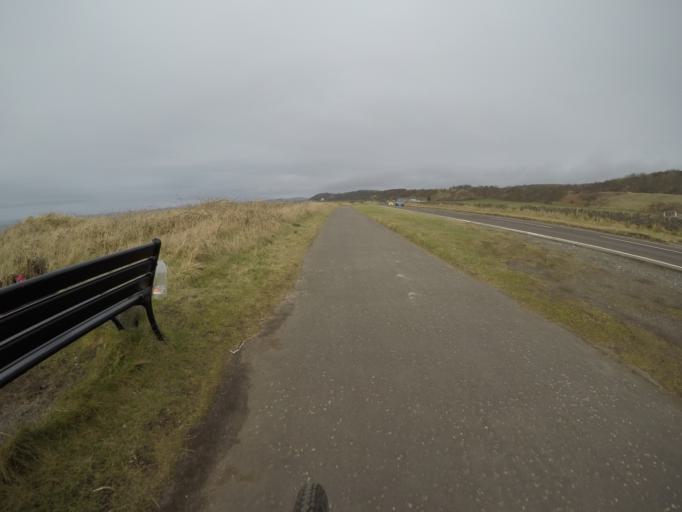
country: GB
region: Scotland
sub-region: North Ayrshire
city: Ardrossan
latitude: 55.6579
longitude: -4.8296
